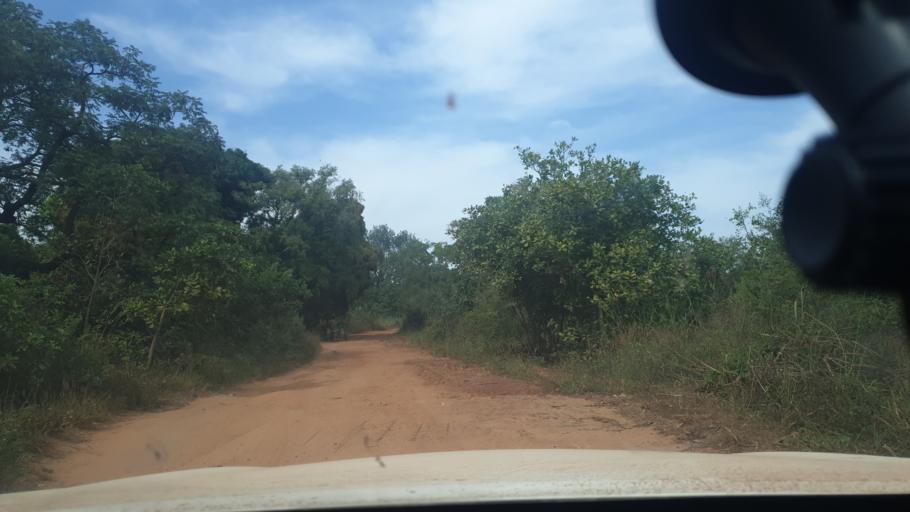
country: ML
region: Sikasso
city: Kadiolo
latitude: 10.8595
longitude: -5.6152
